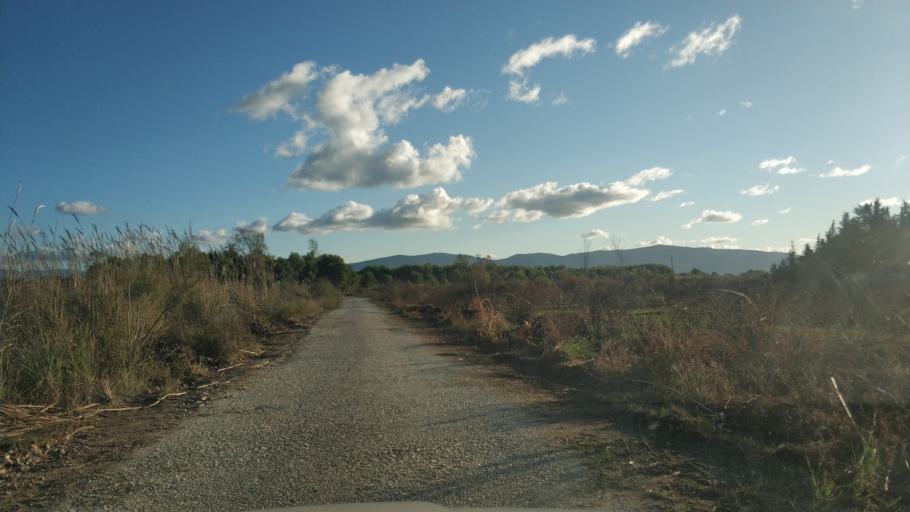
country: AL
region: Vlore
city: Vlore
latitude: 40.5073
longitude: 19.4233
